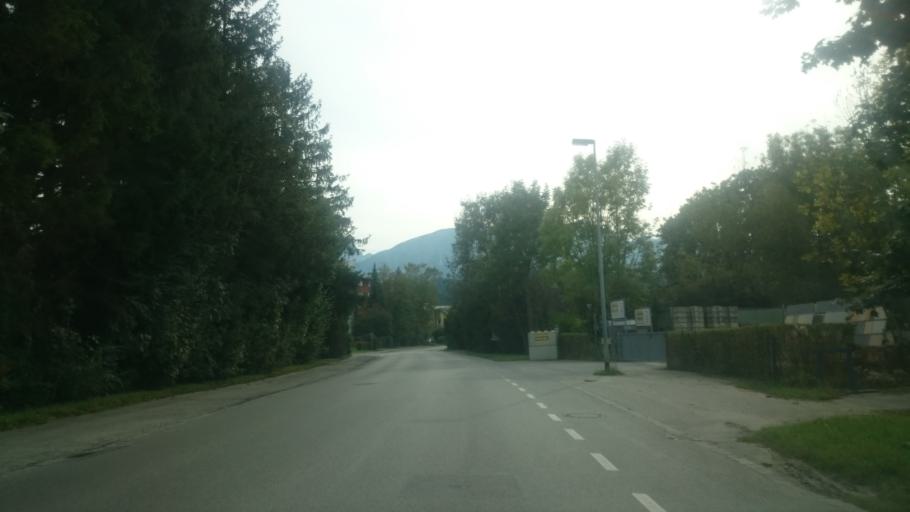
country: DE
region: Bavaria
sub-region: Swabia
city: Fuessen
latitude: 47.5767
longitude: 10.6797
